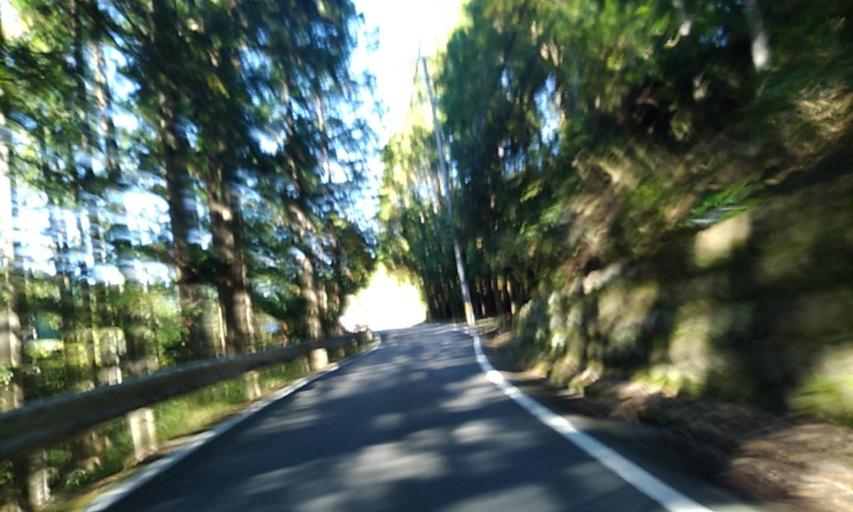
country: JP
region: Wakayama
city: Shingu
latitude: 33.9331
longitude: 135.9773
